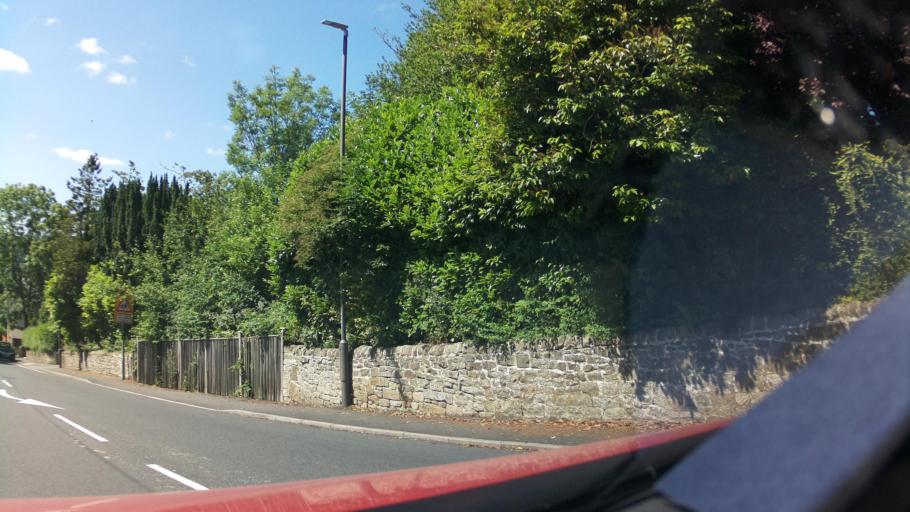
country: GB
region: England
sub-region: Derbyshire
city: Matlock
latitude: 53.1431
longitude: -1.5437
